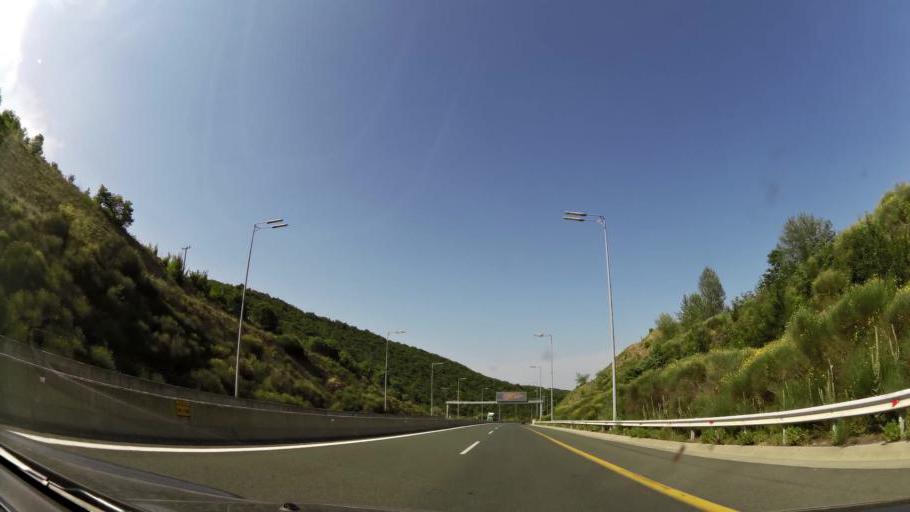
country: GR
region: Central Macedonia
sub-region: Nomos Imathias
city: Veroia
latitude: 40.4450
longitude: 22.1997
